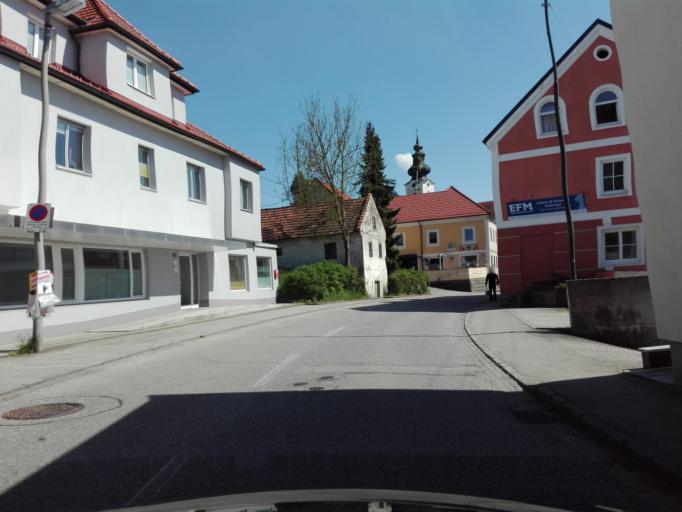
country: AT
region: Upper Austria
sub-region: Politischer Bezirk Grieskirchen
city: Bad Schallerbach
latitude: 48.3166
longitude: 13.9034
